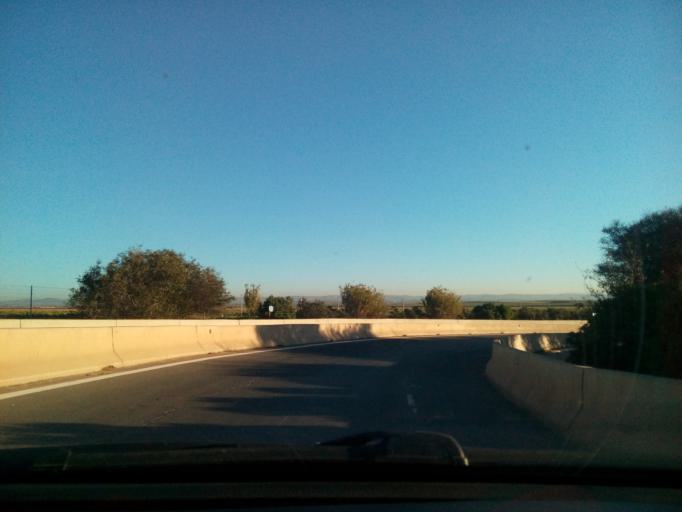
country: DZ
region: Relizane
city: Djidiouia
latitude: 35.8863
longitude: 0.7047
